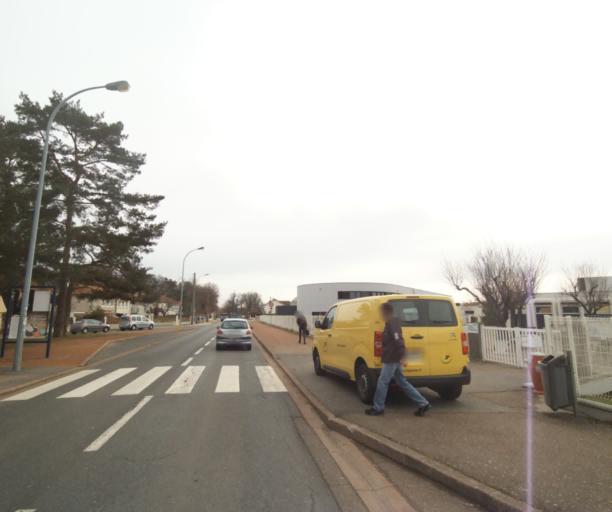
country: FR
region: Rhone-Alpes
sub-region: Departement de la Loire
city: Mably
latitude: 46.0664
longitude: 4.0741
